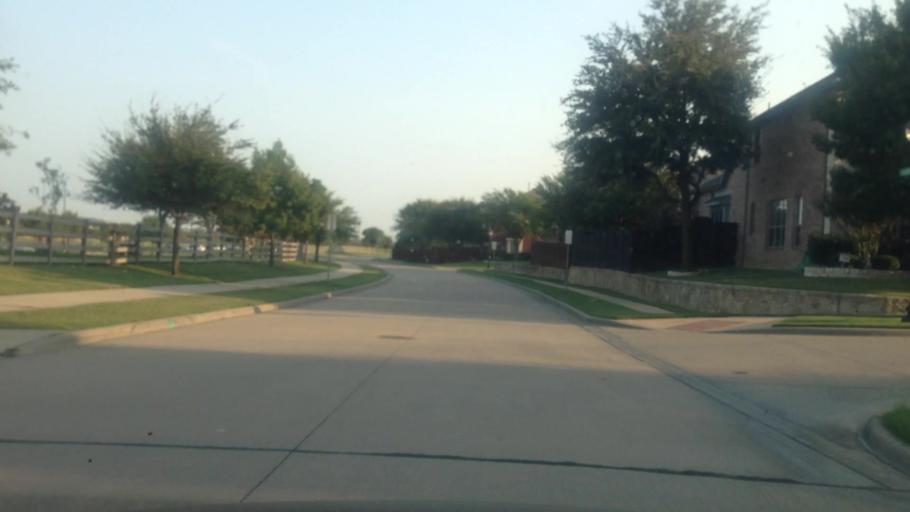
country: US
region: Texas
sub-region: Denton County
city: The Colony
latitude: 33.1281
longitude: -96.8648
